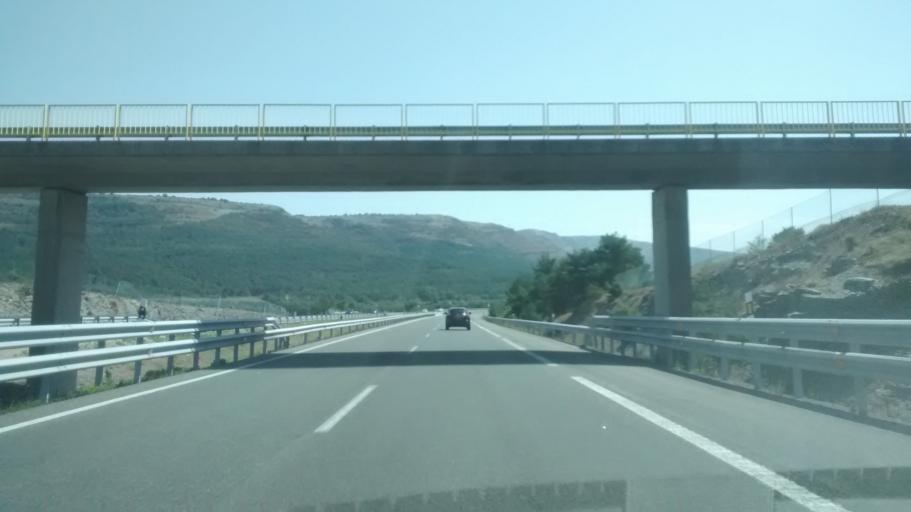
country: ES
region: Basque Country
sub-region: Provincia de Alava
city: Murguia
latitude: 42.9121
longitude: -2.9006
